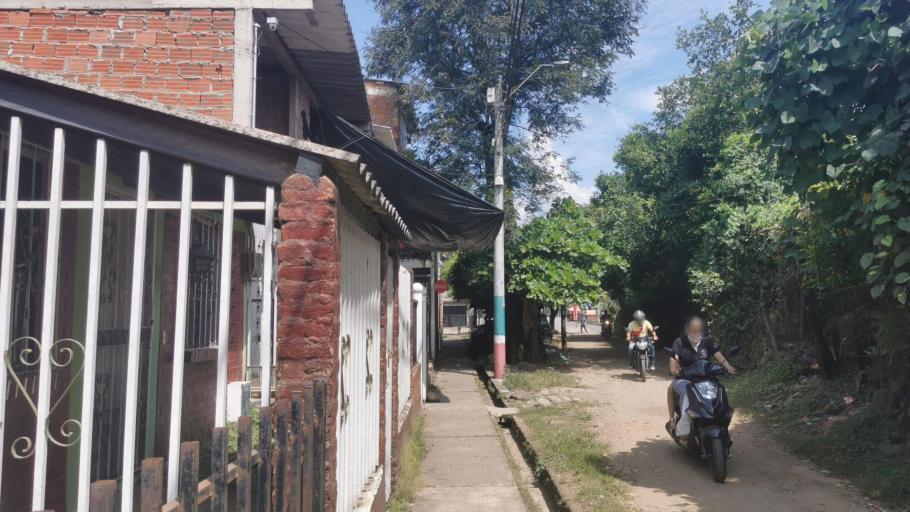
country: CO
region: Valle del Cauca
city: Jamundi
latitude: 3.2555
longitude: -76.5388
